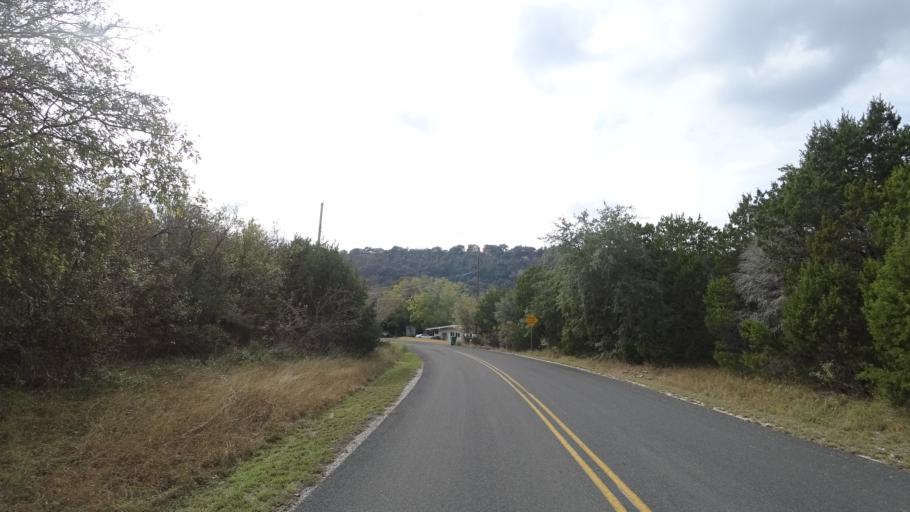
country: US
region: Texas
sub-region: Travis County
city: Hudson Bend
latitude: 30.3855
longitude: -97.9114
